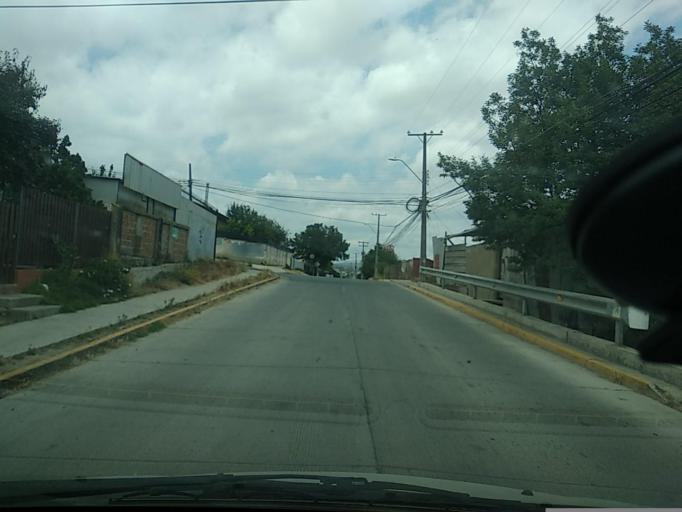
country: CL
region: Valparaiso
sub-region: Provincia de Marga Marga
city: Villa Alemana
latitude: -33.0348
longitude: -71.4043
